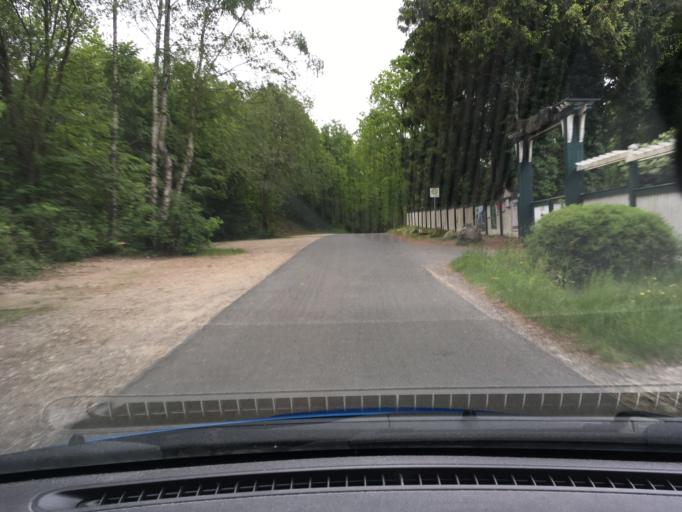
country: DE
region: Lower Saxony
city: Bispingen
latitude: 53.0706
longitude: 10.0098
